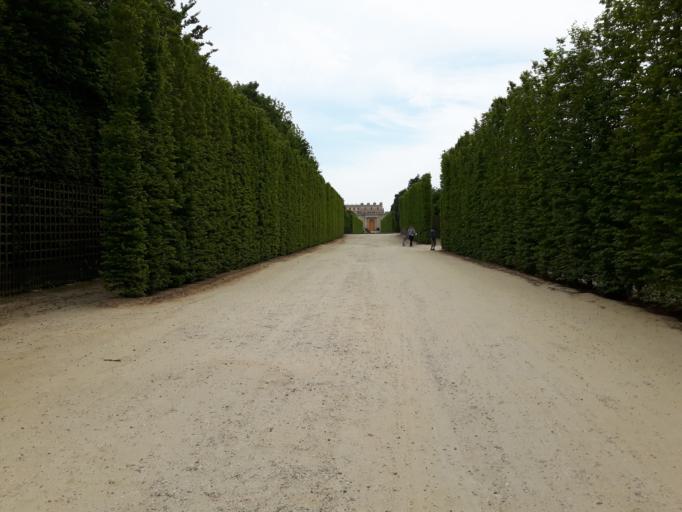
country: FR
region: Ile-de-France
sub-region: Departement des Yvelines
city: Le Chesnay
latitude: 48.8046
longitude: 2.1139
